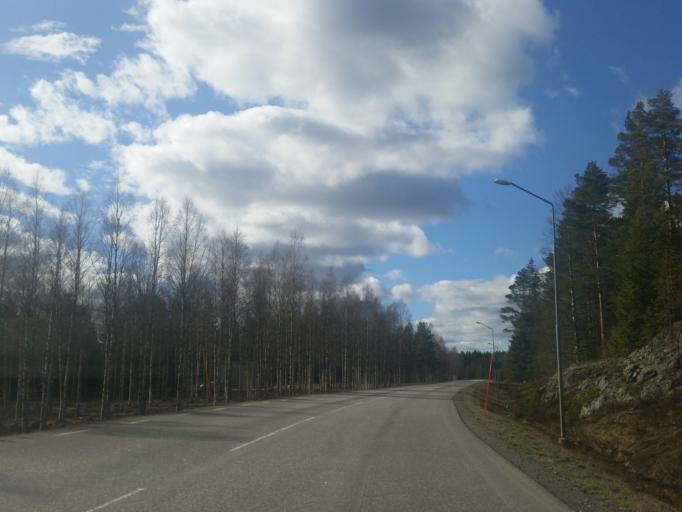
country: SE
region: Vaesterbotten
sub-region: Robertsfors Kommun
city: Robertsfors
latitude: 64.1977
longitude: 20.8370
